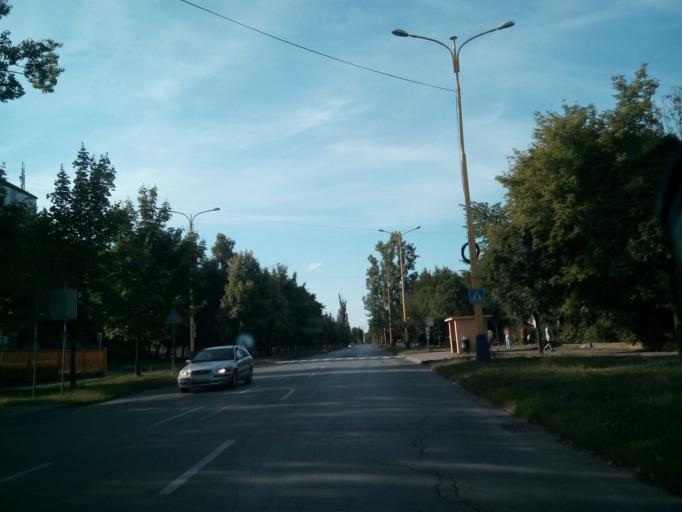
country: SK
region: Kosicky
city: Kosice
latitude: 48.6301
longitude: 21.1727
